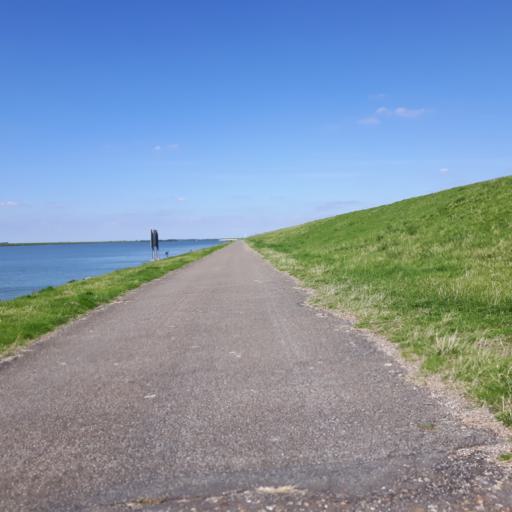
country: NL
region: North Brabant
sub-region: Gemeente Bergen op Zoom
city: Bergen op Zoom
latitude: 51.4593
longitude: 4.2327
